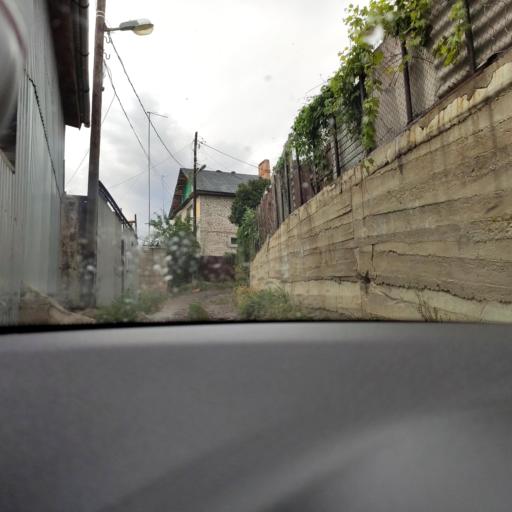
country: RU
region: Samara
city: Samara
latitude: 53.1728
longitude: 50.1577
